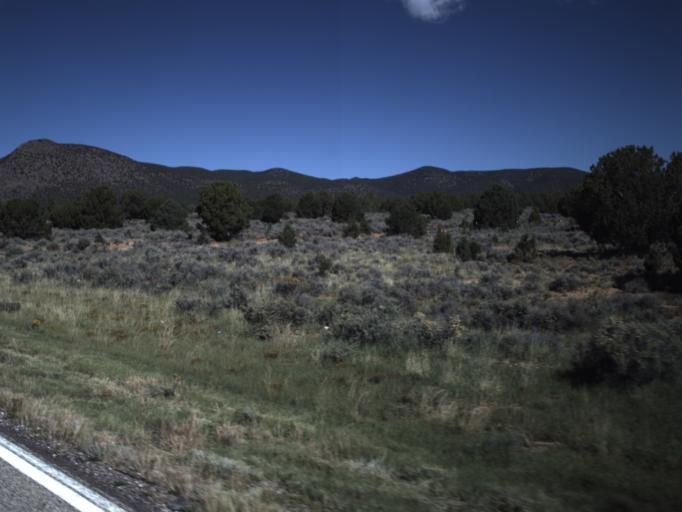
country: US
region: Utah
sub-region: Washington County
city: Enterprise
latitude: 37.6386
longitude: -113.4356
